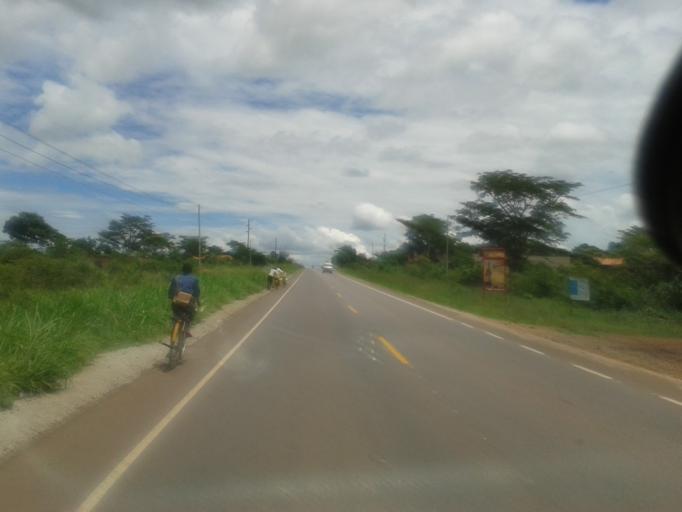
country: UG
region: Western Region
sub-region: Kiryandongo District
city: Kiryandongo
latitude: 1.8695
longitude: 32.0538
